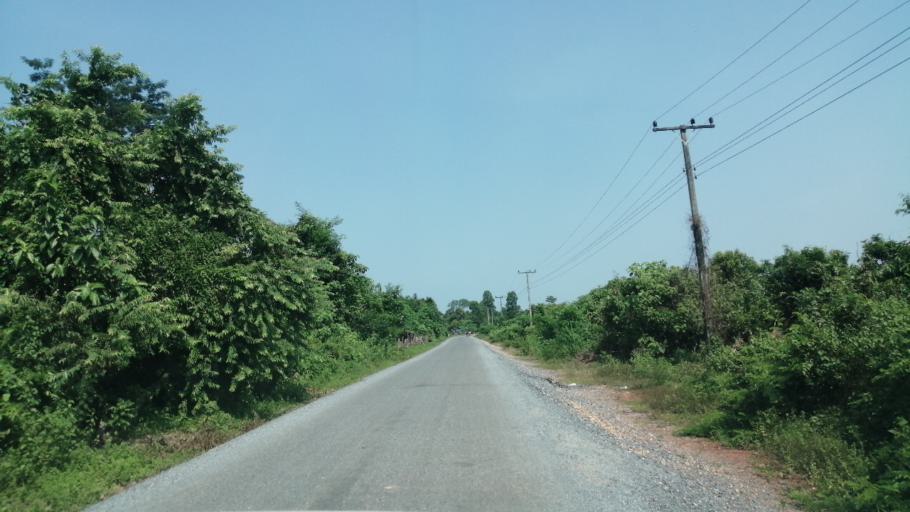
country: LA
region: Bolikhamxai
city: Bolikhan
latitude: 18.4504
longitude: 103.8082
